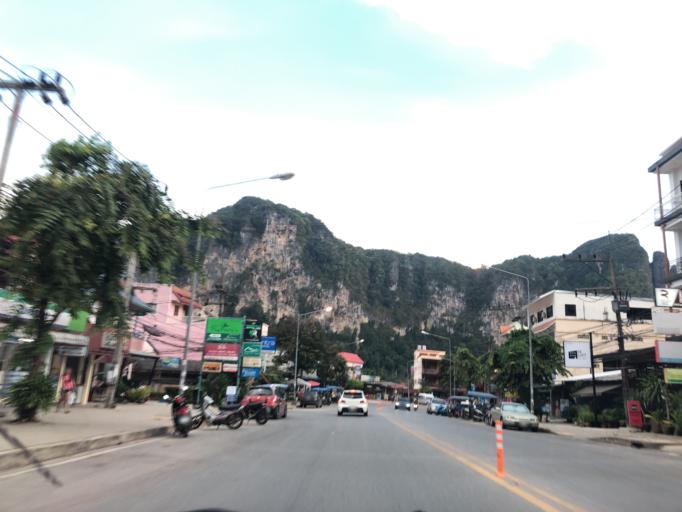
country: TH
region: Phangnga
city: Ban Ao Nang
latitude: 8.0370
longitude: 98.8336
